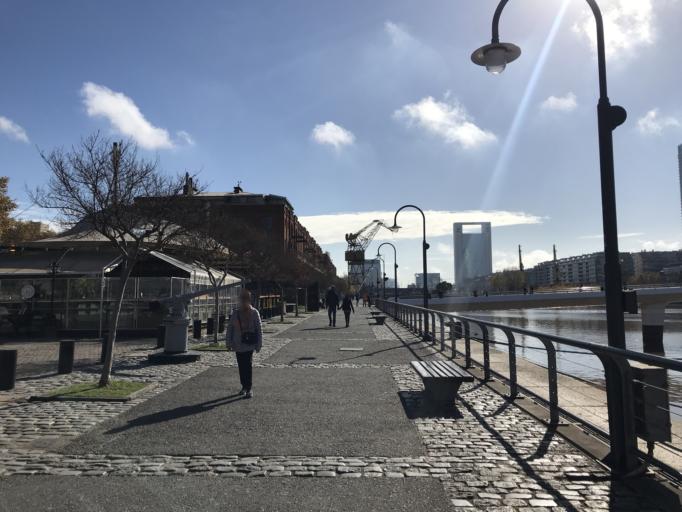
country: AR
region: Buenos Aires F.D.
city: Buenos Aires
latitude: -34.6090
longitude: -58.3659
